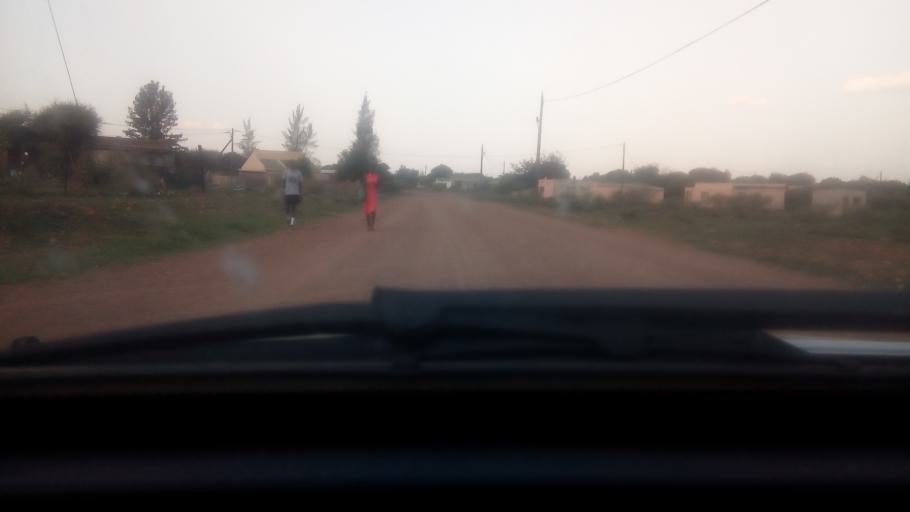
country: BW
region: Kgatleng
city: Bokaa
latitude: -24.4290
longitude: 26.0130
